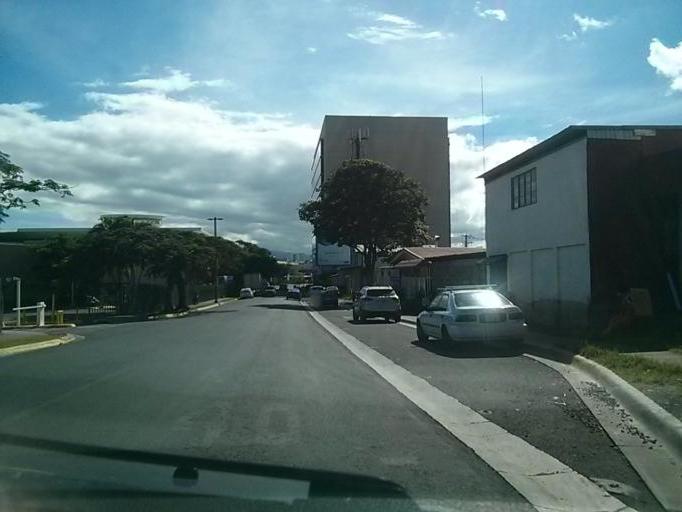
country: CR
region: San Jose
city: San Rafael
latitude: 9.9435
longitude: -84.1524
